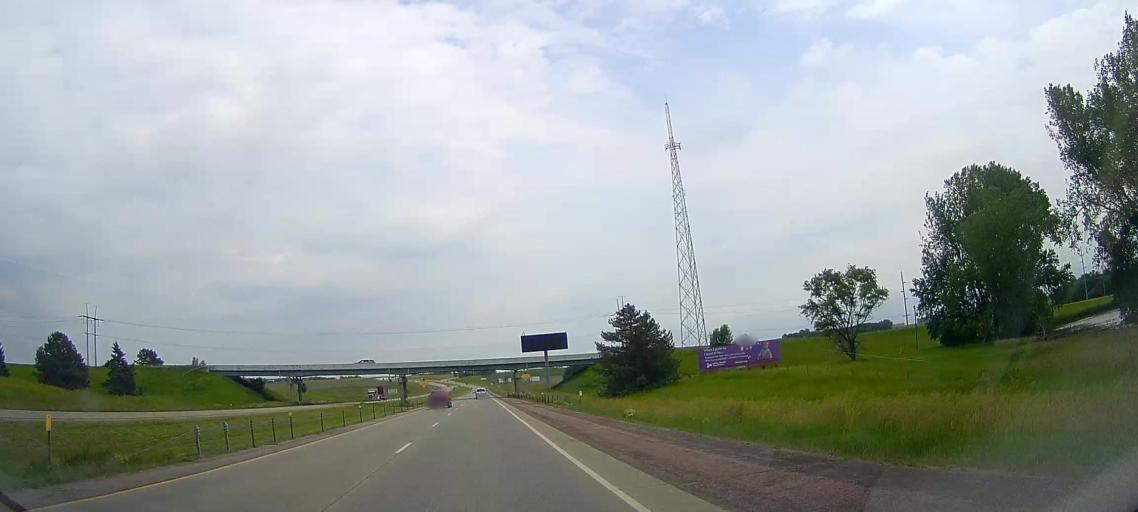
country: US
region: South Dakota
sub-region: Minnehaha County
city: Crooks
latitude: 43.6086
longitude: -96.8118
